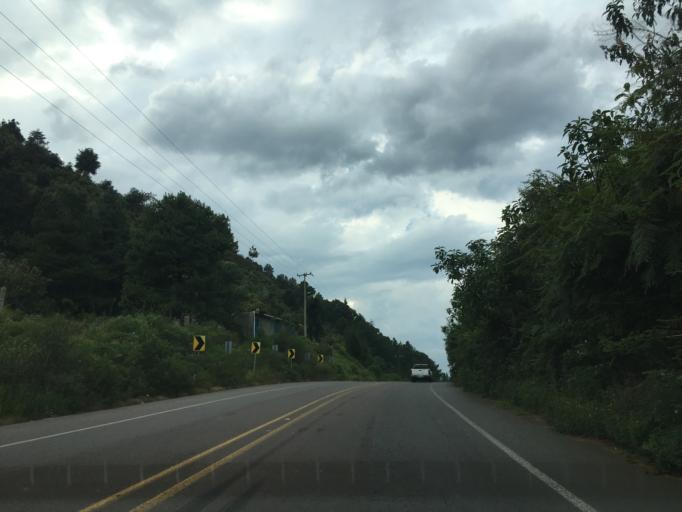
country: MX
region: Michoacan
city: Angahuan
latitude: 19.5270
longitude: -102.1897
